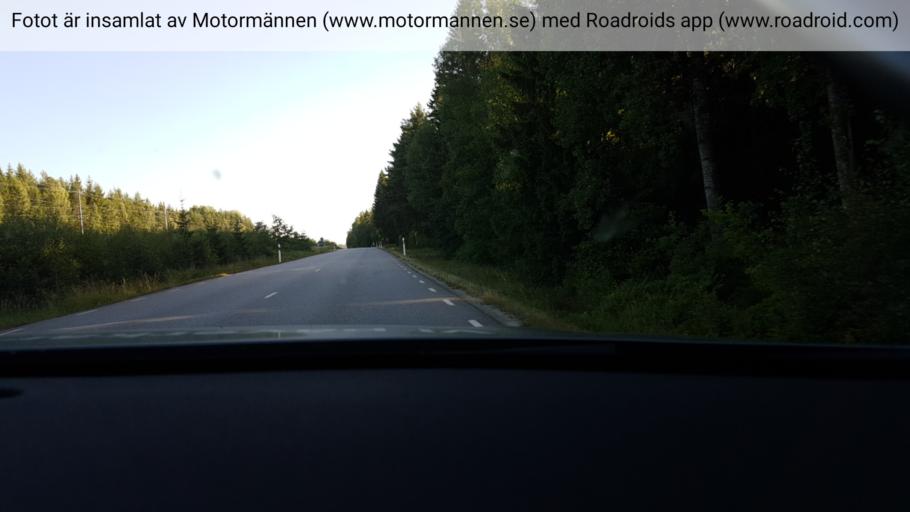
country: SE
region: Vaestra Goetaland
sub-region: Toreboda Kommun
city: Toereboda
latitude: 58.6662
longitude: 14.0921
